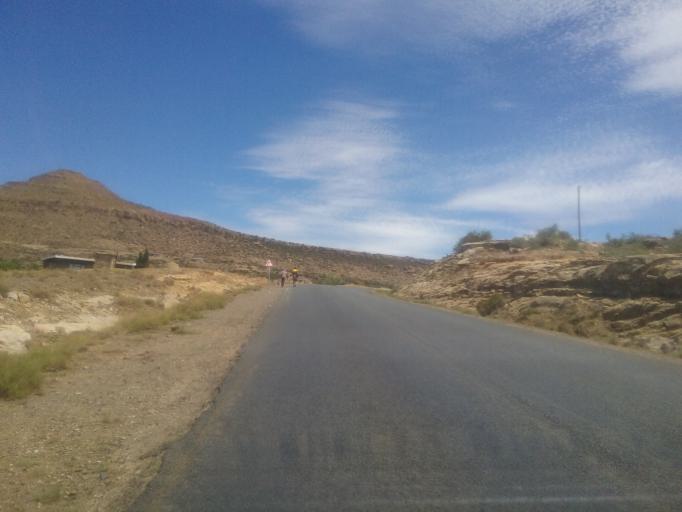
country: LS
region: Mohale's Hoek District
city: Mohale's Hoek
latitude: -30.0765
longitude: 27.4266
